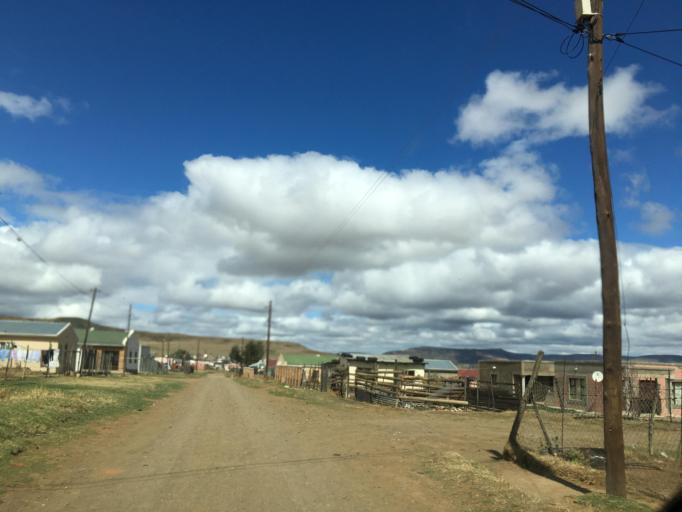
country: ZA
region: Eastern Cape
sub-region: Chris Hani District Municipality
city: Cala
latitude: -31.5326
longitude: 27.7027
